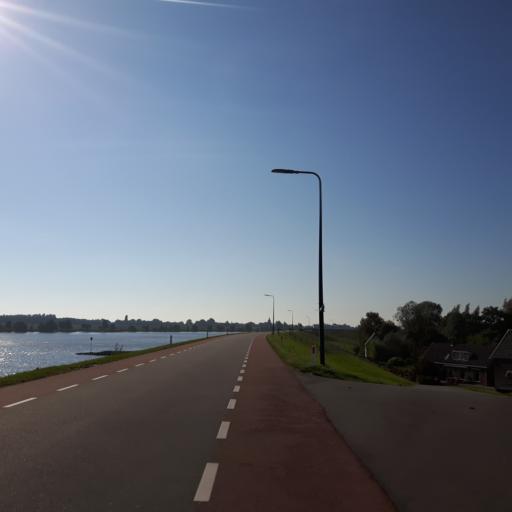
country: NL
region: South Holland
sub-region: Molenwaard
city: Liesveld
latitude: 51.9376
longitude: 4.8263
